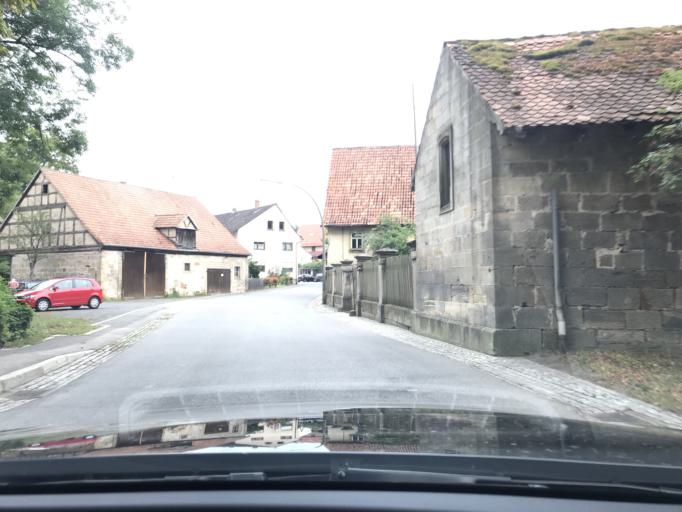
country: DE
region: Bavaria
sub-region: Regierungsbezirk Unterfranken
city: Burgpreppach
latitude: 50.1404
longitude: 10.6513
